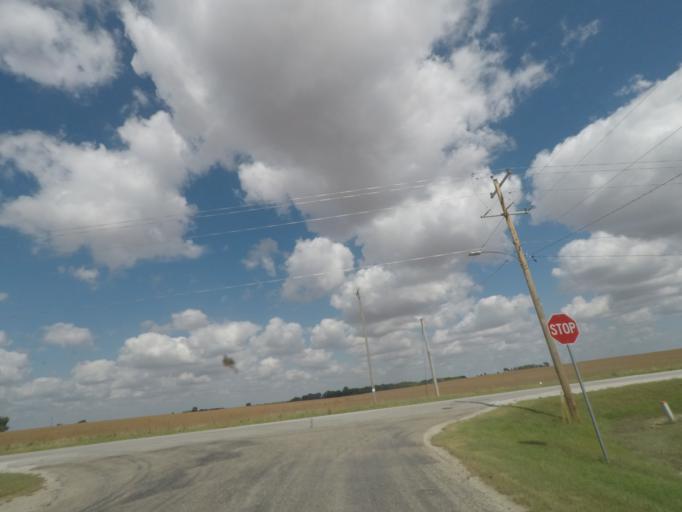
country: US
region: Iowa
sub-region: Story County
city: Nevada
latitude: 42.0223
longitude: -93.3159
